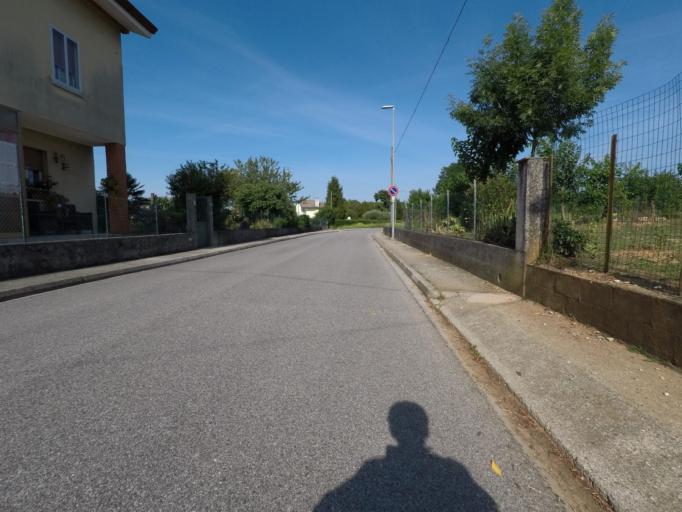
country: IT
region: Friuli Venezia Giulia
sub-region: Provincia di Udine
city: Pasian di Prato
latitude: 46.0506
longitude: 13.1847
